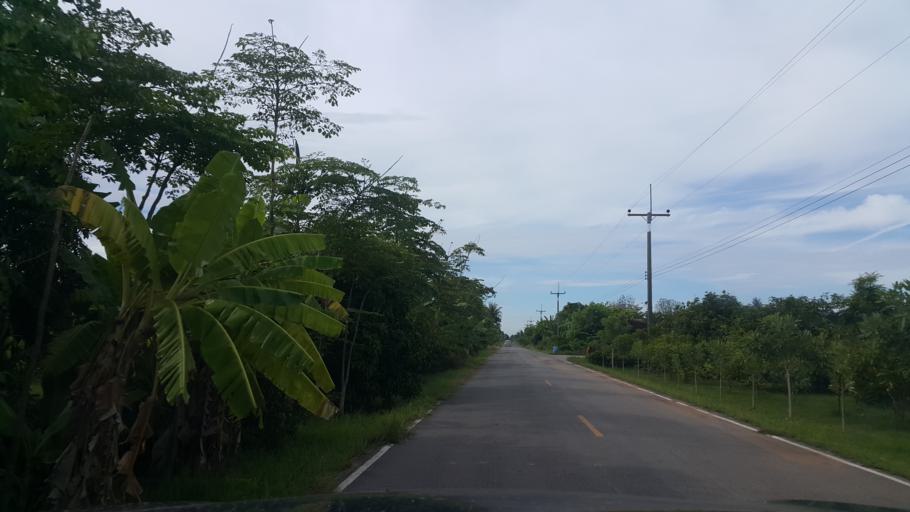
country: TH
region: Sukhothai
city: Sawankhalok
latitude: 17.2698
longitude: 99.9076
